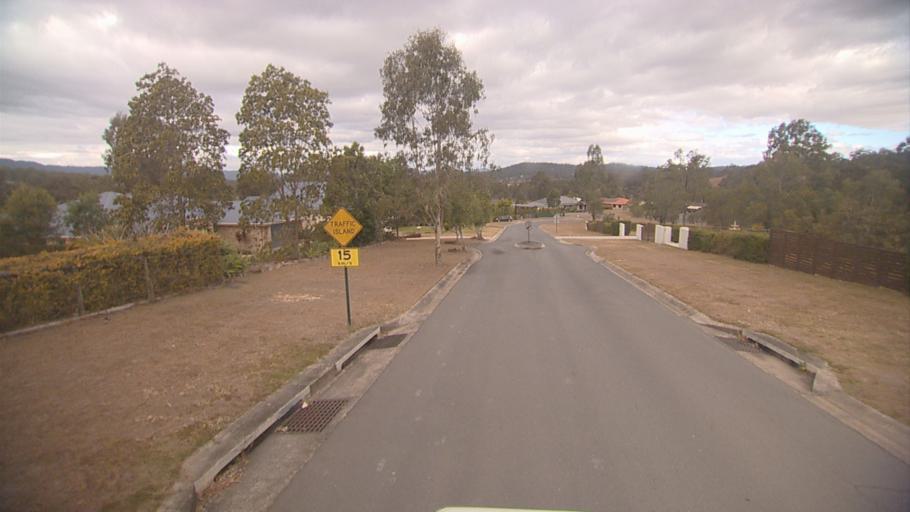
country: AU
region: Queensland
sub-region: Logan
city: Cedar Vale
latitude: -27.8730
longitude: 153.0689
